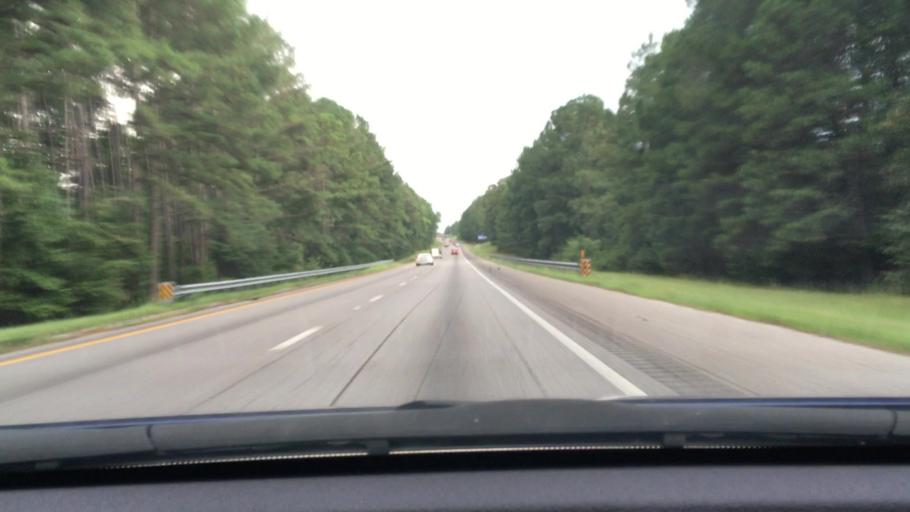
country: US
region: South Carolina
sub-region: Kershaw County
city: Elgin
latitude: 34.1521
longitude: -80.7379
